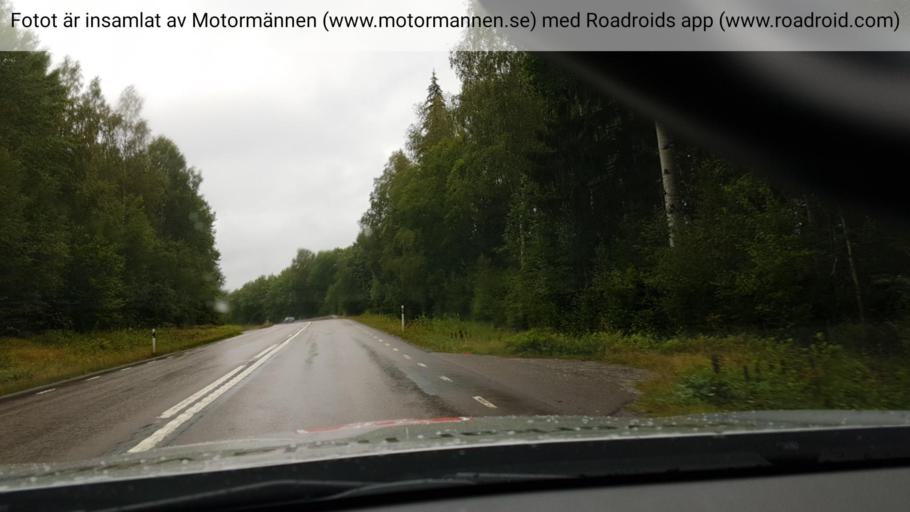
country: SE
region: Vaestra Goetaland
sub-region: Bengtsfors Kommun
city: Billingsfors
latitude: 58.9406
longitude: 12.1126
